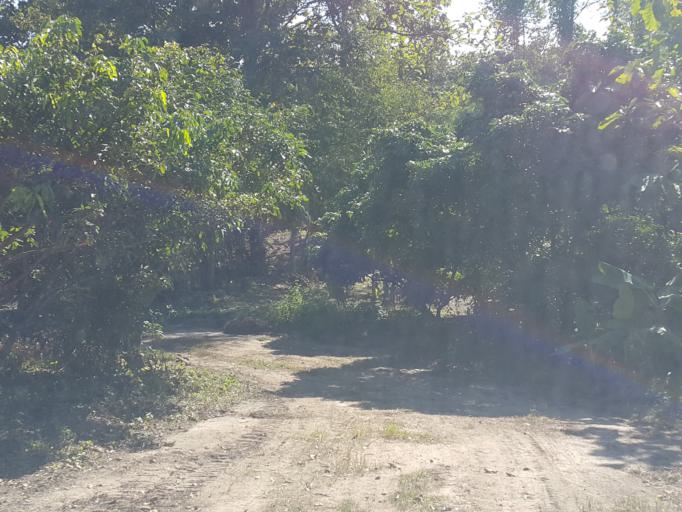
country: TH
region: Chiang Mai
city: Mae Taeng
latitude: 18.9562
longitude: 98.9007
